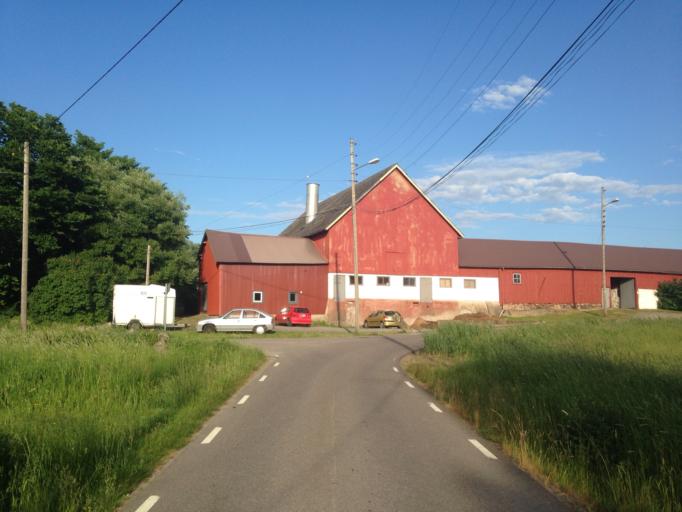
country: SE
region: Vaestra Goetaland
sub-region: Goteborg
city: Majorna
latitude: 57.8012
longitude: 11.8868
